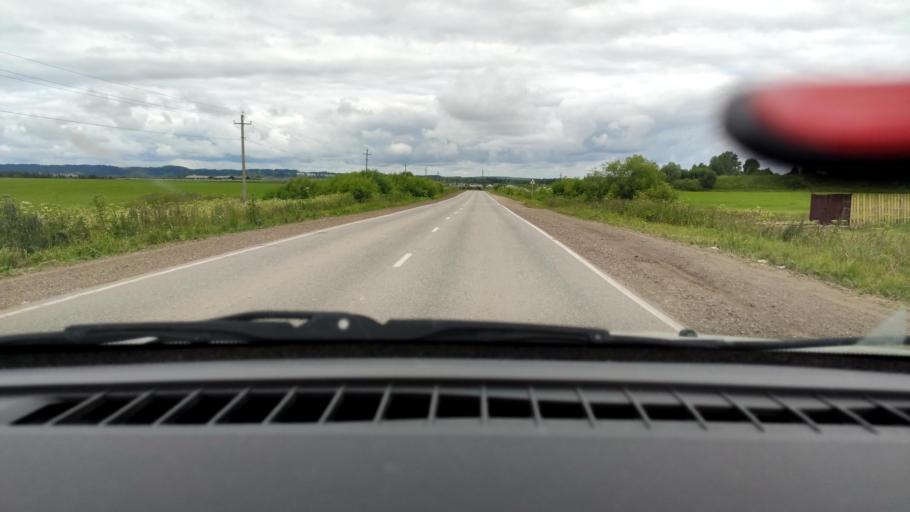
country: RU
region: Perm
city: Ust'-Kachka
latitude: 58.0705
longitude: 55.6254
